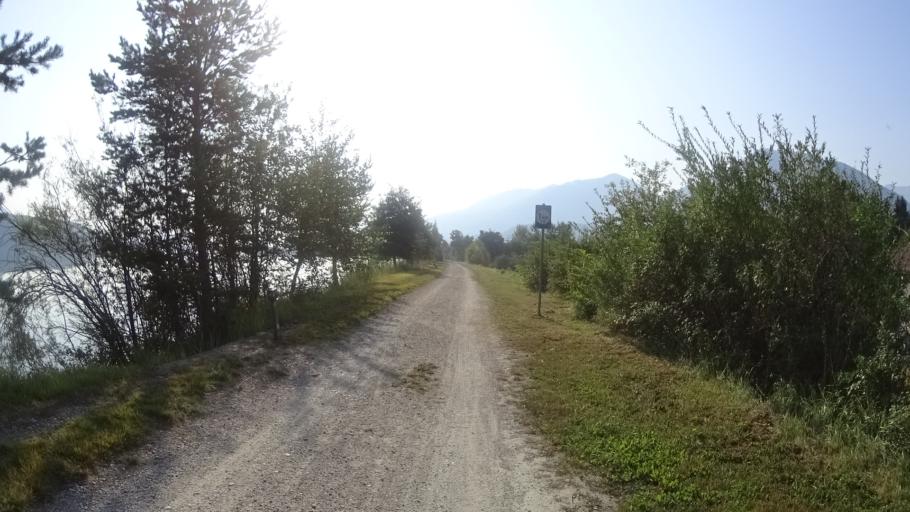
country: AT
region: Carinthia
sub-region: Politischer Bezirk Klagenfurt Land
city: Ludmannsdorf
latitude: 46.5298
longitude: 14.1463
